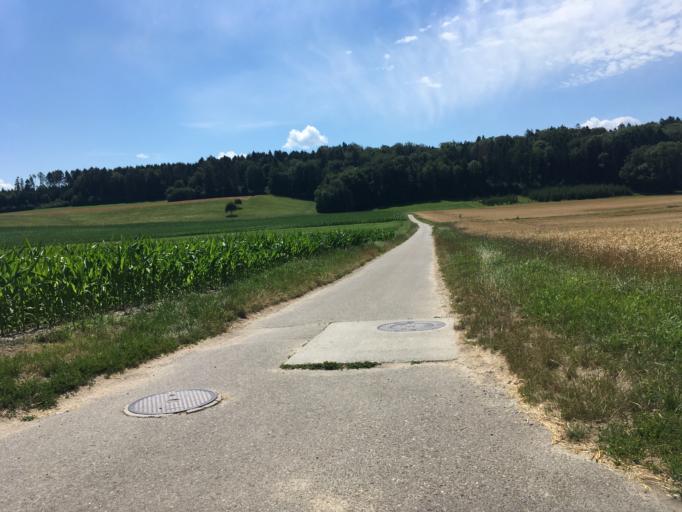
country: CH
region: Neuchatel
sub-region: Neuchatel District
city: Saint-Blaise
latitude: 46.9408
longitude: 6.9986
